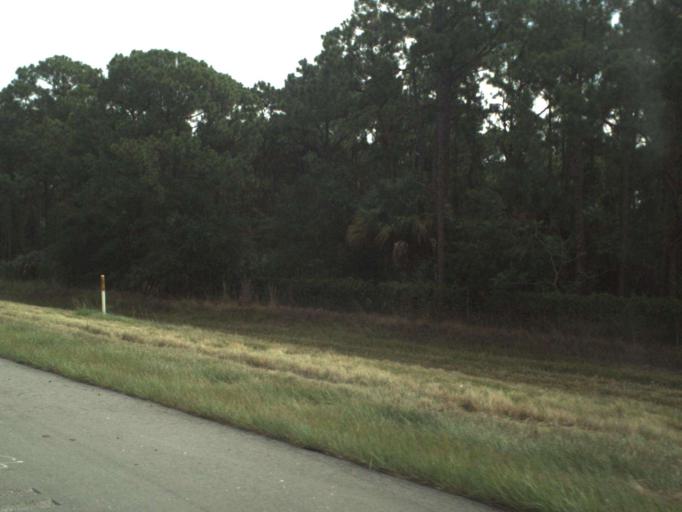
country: US
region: Florida
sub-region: Saint Lucie County
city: Fort Pierce South
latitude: 27.4312
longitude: -80.3882
